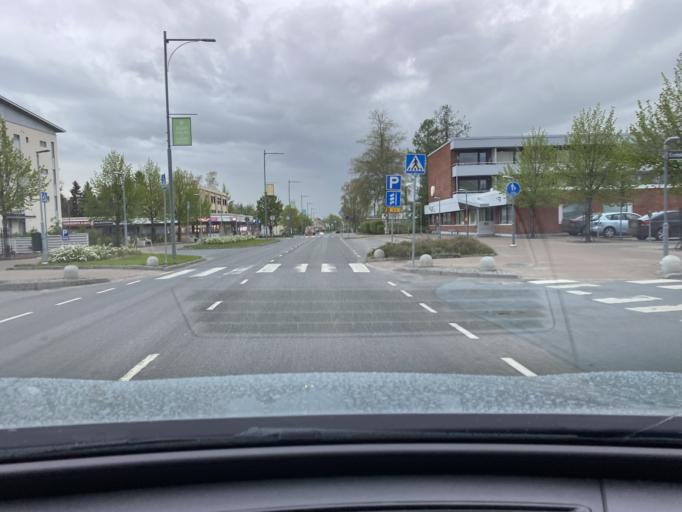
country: FI
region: Varsinais-Suomi
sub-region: Salo
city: Somero
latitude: 60.6309
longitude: 23.5130
